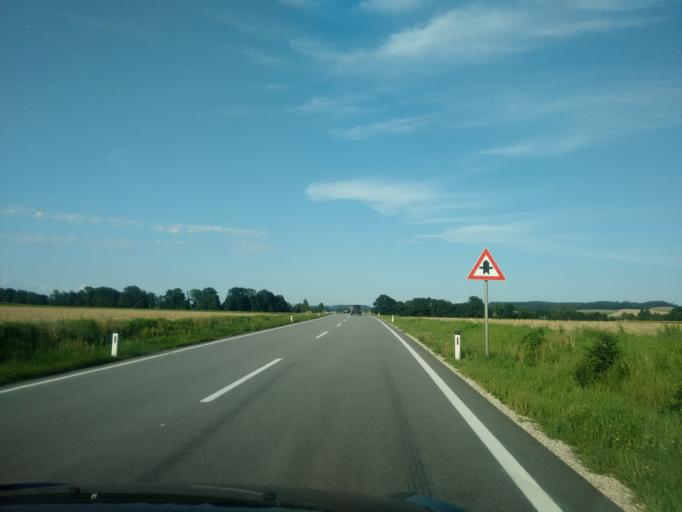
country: DE
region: Bavaria
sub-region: Lower Bavaria
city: Bad Fussing
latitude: 48.3035
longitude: 13.3380
